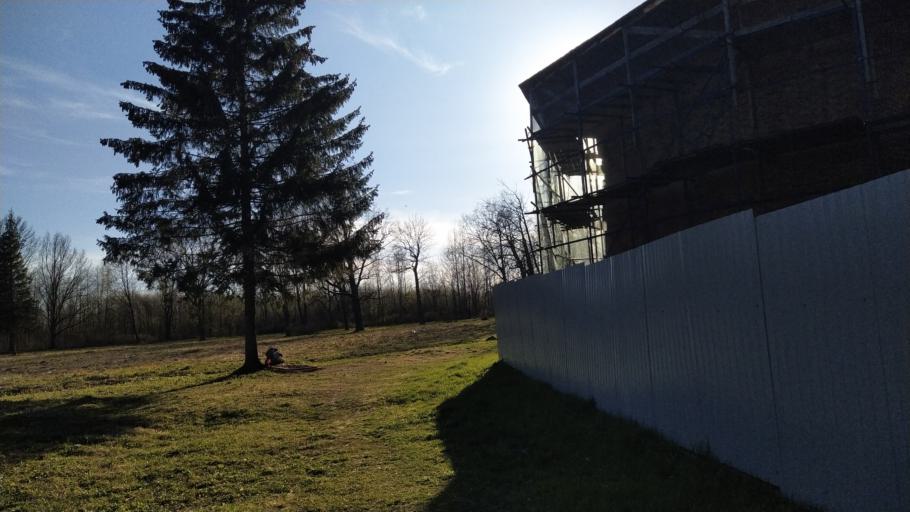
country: RU
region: St.-Petersburg
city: Aleksandrovskaya
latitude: 59.7086
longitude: 30.3448
